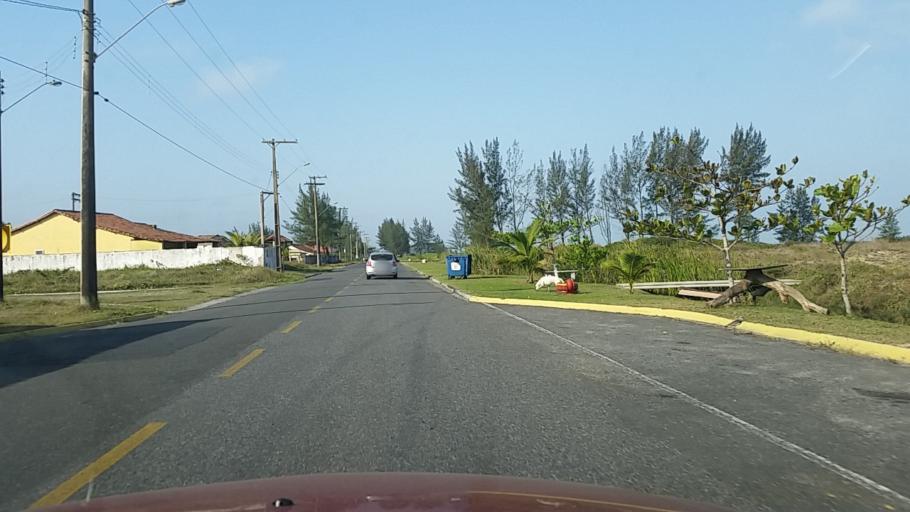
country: BR
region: Sao Paulo
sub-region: Iguape
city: Iguape
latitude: -24.7931
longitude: -47.6189
